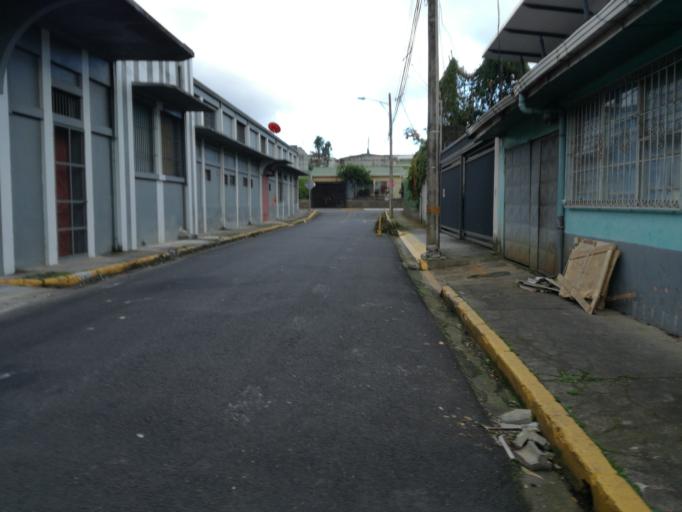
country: CR
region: San Jose
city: San Pedro
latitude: 9.9330
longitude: -84.0502
